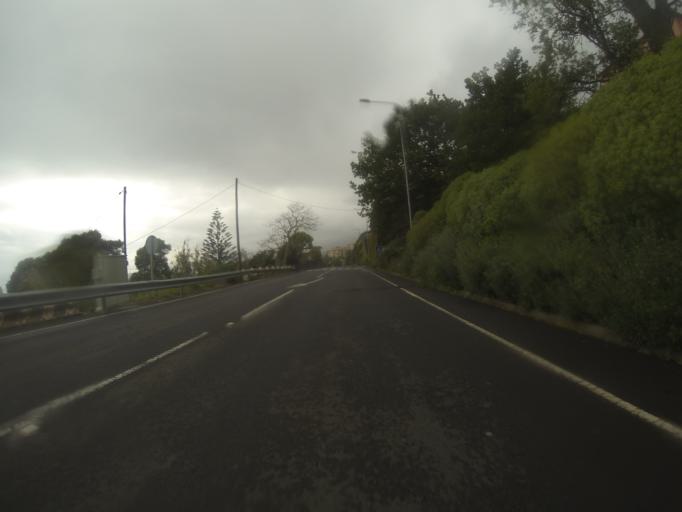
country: PT
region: Madeira
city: Canico
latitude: 32.6485
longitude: -16.8697
